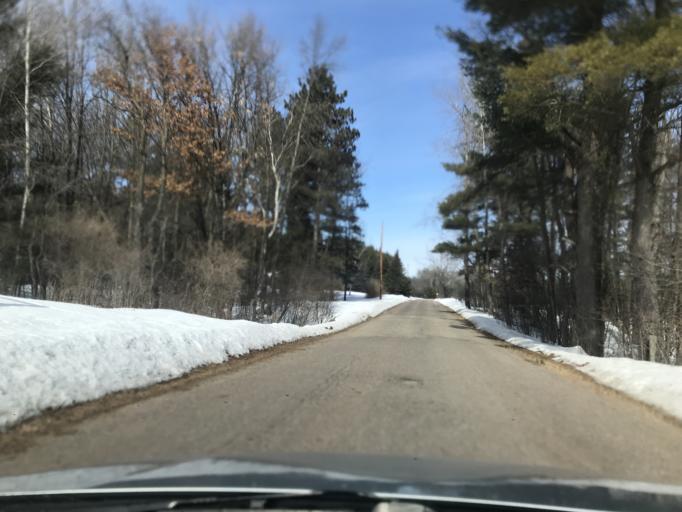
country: US
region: Wisconsin
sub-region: Marinette County
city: Peshtigo
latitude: 45.2240
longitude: -87.9624
